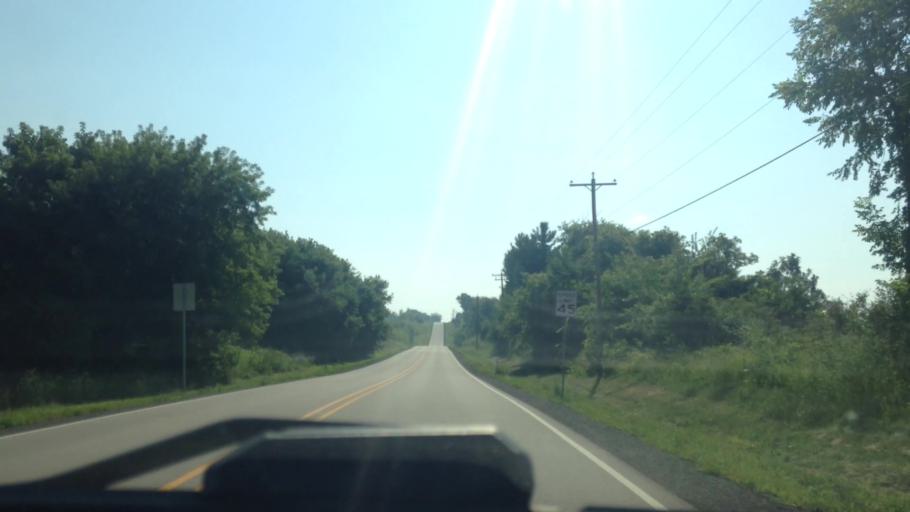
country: US
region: Wisconsin
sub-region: Waukesha County
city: Merton
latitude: 43.1631
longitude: -88.2779
